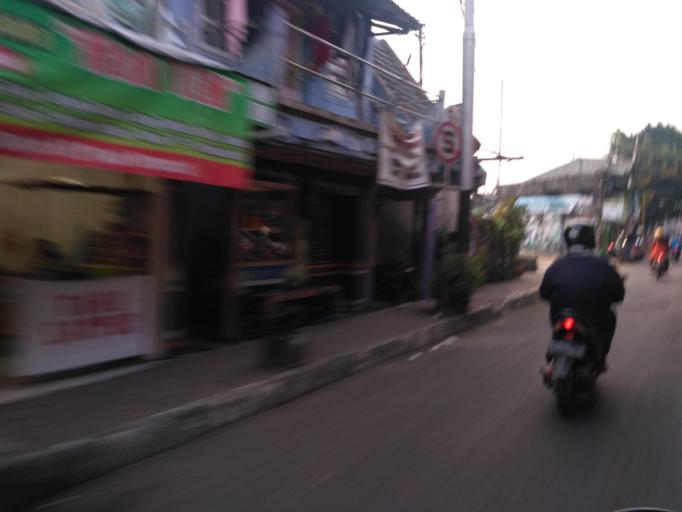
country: ID
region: East Java
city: Malang
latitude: -7.9946
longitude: 112.6332
